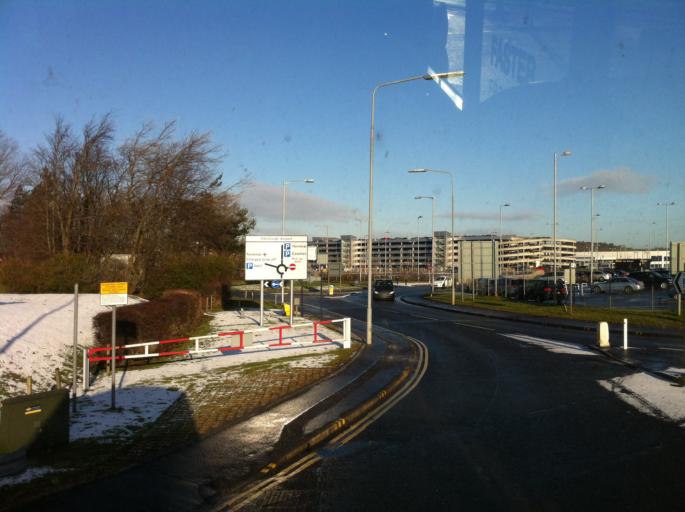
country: GB
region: Scotland
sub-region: Edinburgh
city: Ratho
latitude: 55.9443
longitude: -3.3614
